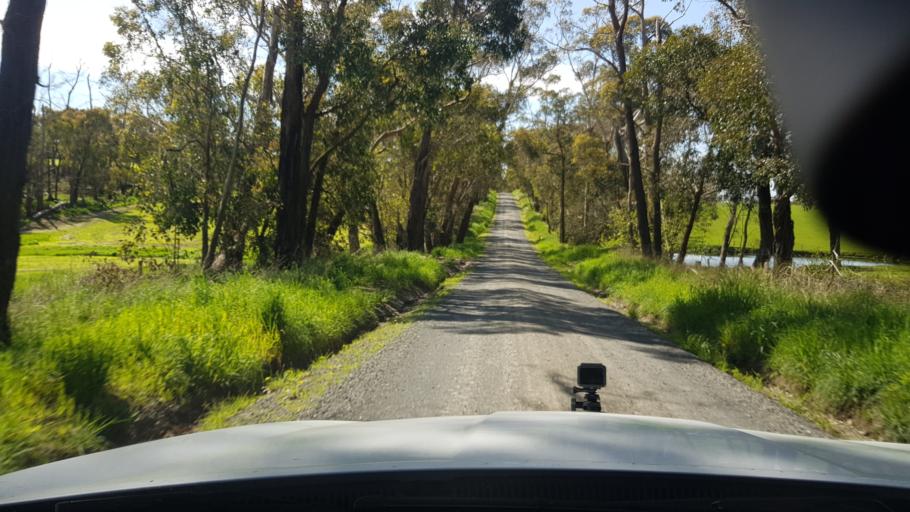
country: AU
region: Victoria
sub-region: Latrobe
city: Moe
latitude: -38.1492
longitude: 146.1298
